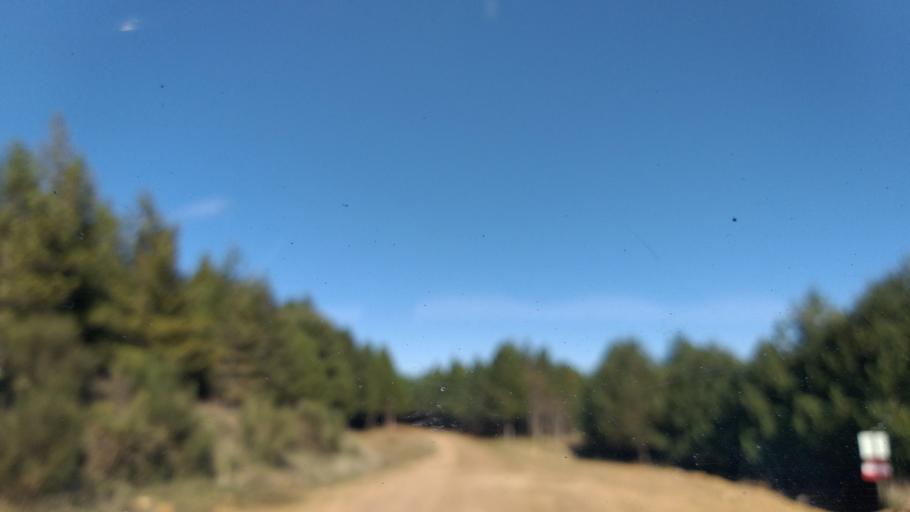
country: PT
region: Guarda
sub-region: Manteigas
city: Manteigas
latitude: 40.5078
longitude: -7.4625
